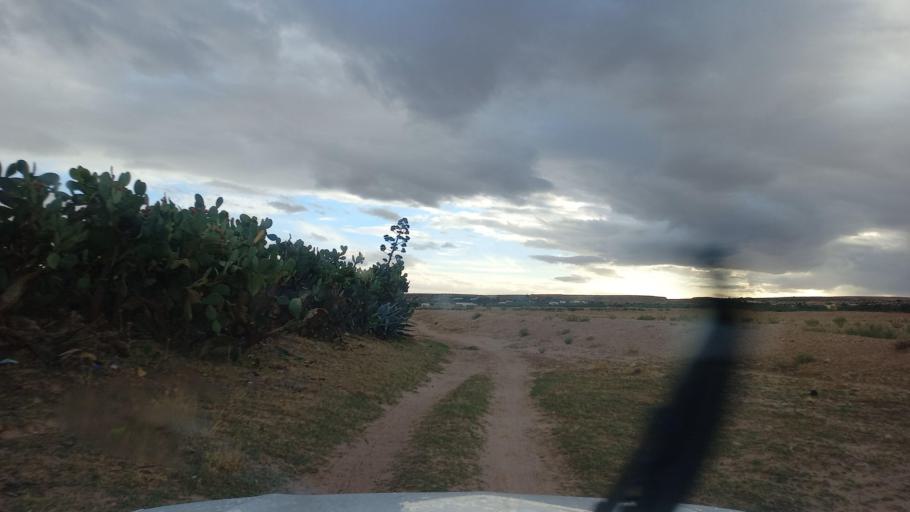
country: TN
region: Al Qasrayn
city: Kasserine
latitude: 35.2715
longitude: 8.9368
